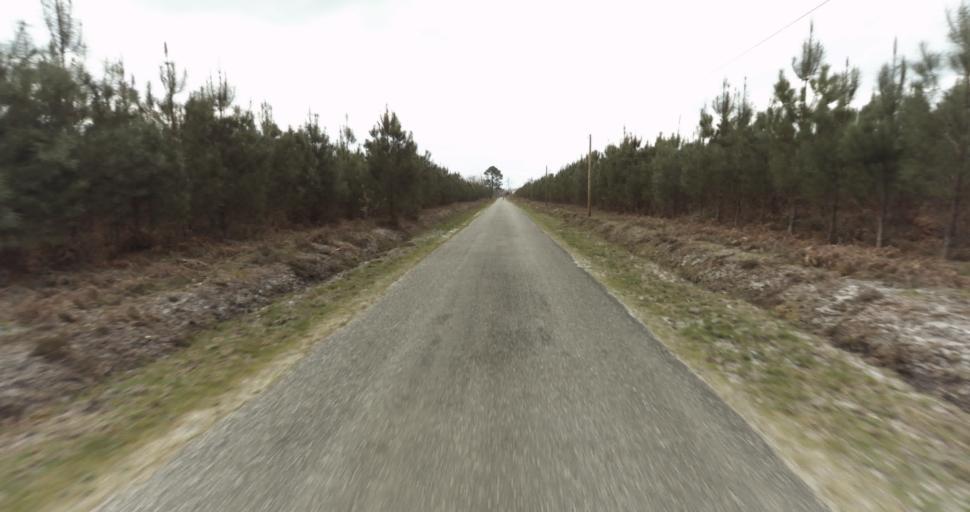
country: FR
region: Aquitaine
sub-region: Departement des Landes
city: Sarbazan
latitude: 44.0089
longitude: -0.3367
